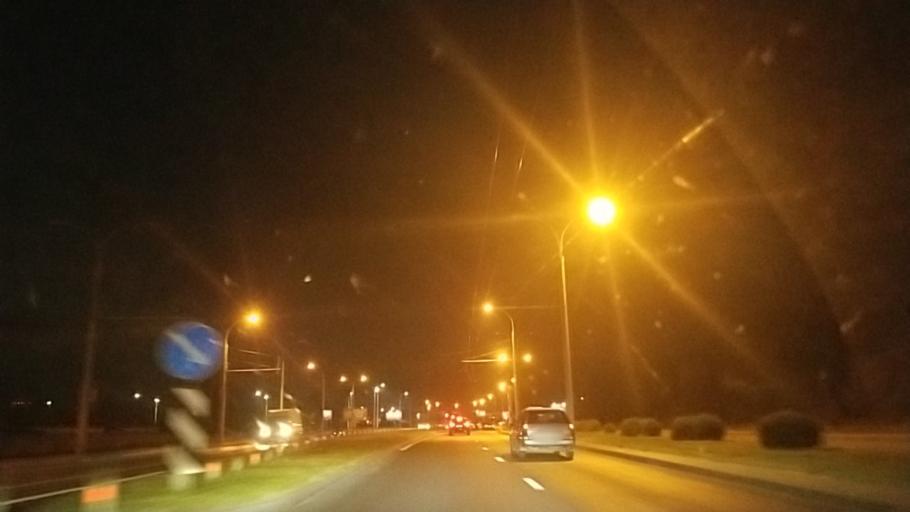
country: BY
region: Brest
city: Brest
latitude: 52.0816
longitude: 23.7710
